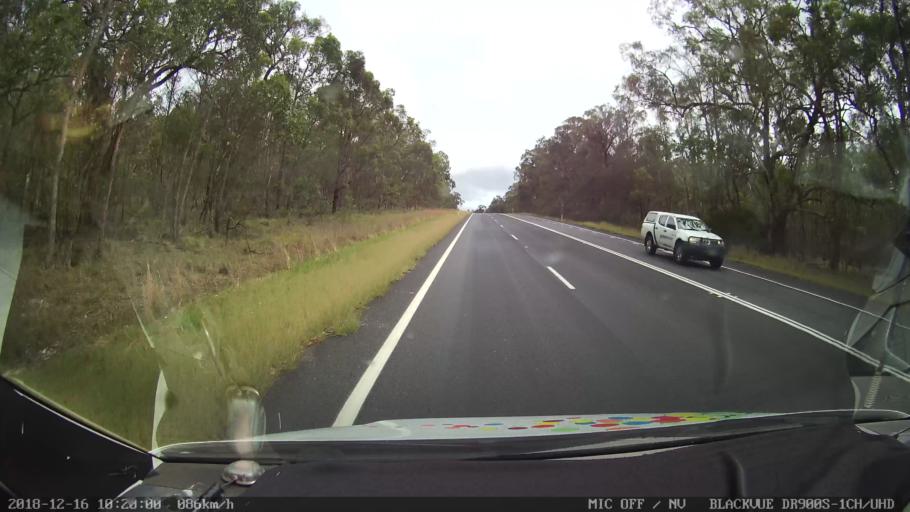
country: AU
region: New South Wales
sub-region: Tenterfield Municipality
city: Carrolls Creek
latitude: -29.2258
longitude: 152.0092
